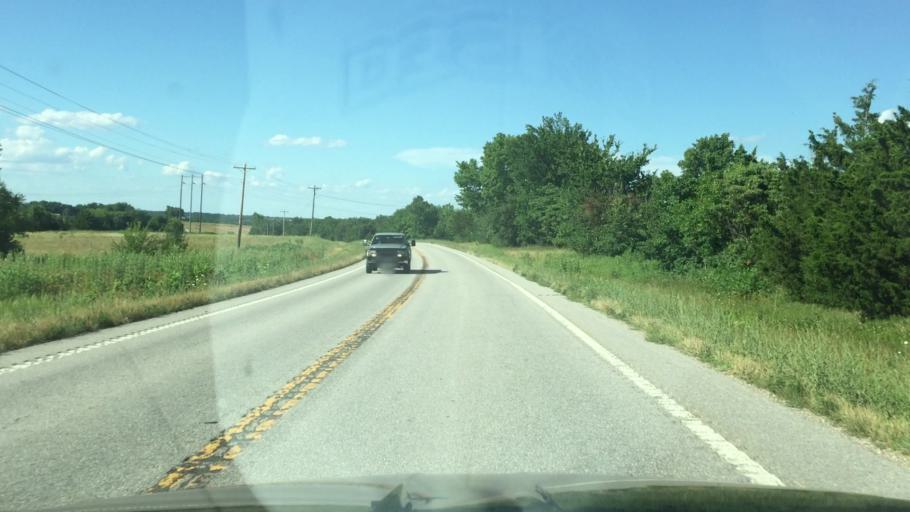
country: US
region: Missouri
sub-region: Morgan County
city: Versailles
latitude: 38.5274
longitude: -92.7996
